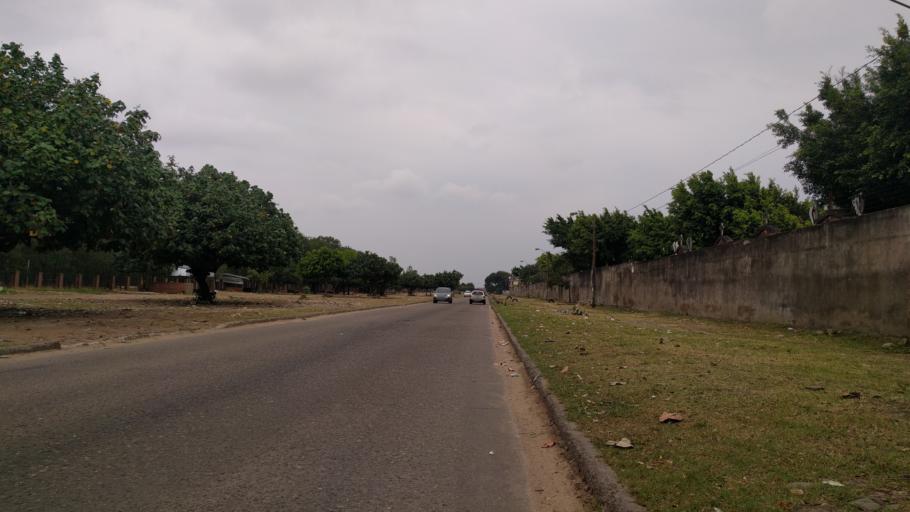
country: BO
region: Santa Cruz
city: Santa Cruz de la Sierra
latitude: -17.8219
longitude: -63.1957
